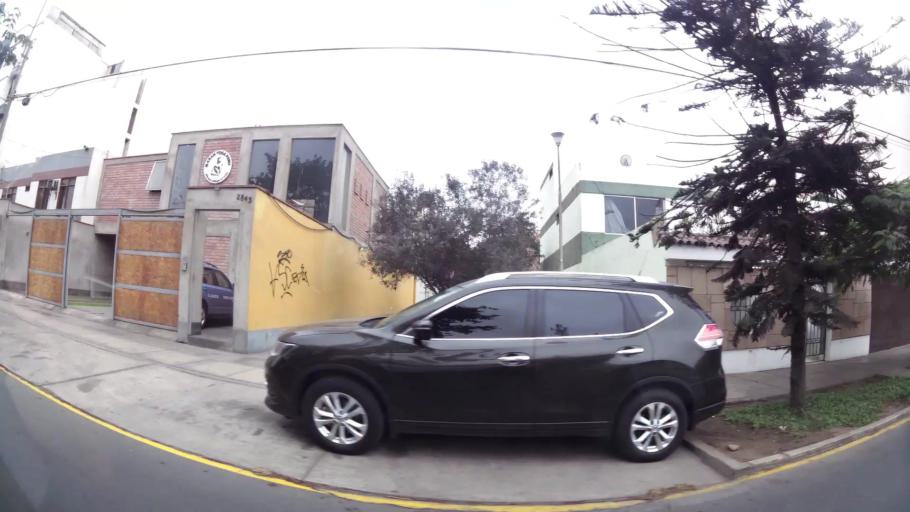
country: PE
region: Lima
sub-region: Lima
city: San Luis
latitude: -12.1053
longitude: -76.9928
